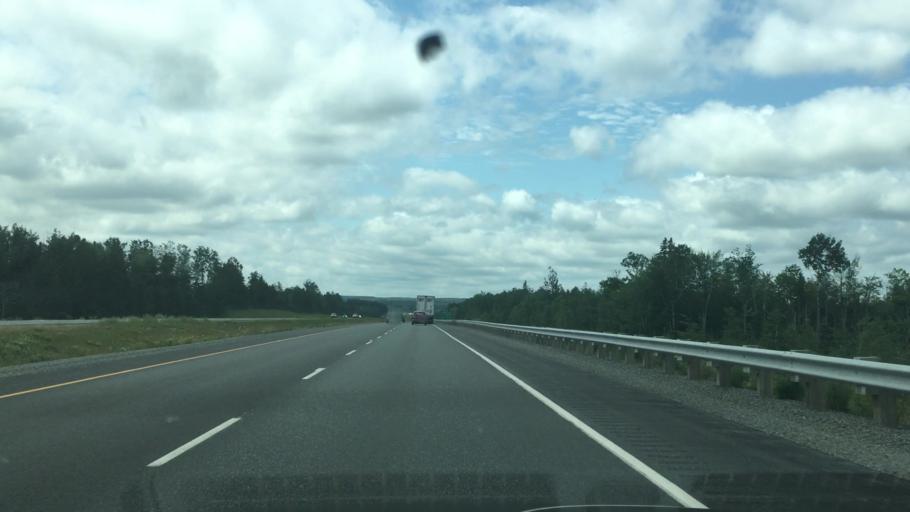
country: CA
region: Nova Scotia
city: Springhill
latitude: 45.7042
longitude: -63.9753
